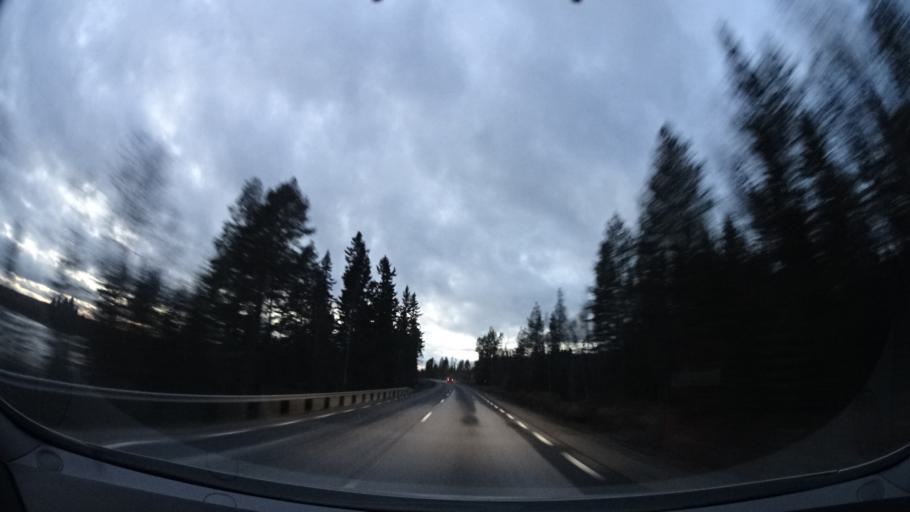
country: SE
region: Vaesterbotten
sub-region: Asele Kommun
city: Asele
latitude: 64.1885
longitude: 17.1663
